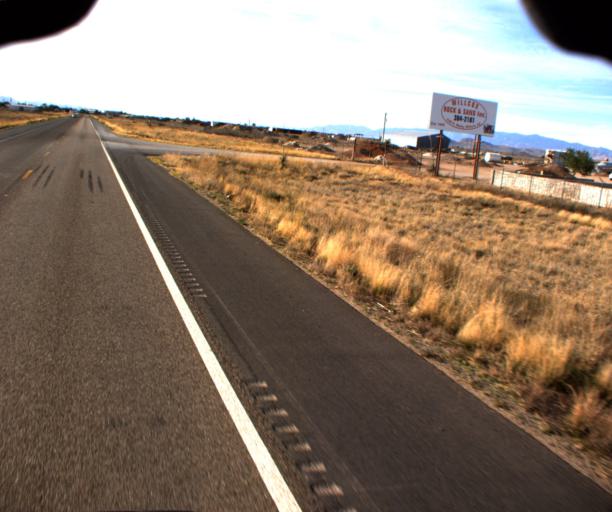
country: US
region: Arizona
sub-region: Cochise County
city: Willcox
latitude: 32.2391
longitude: -109.8113
